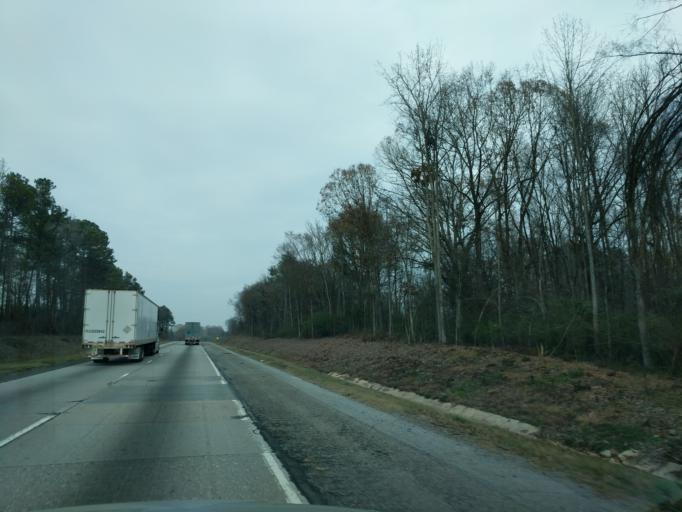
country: US
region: Georgia
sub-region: Jackson County
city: Commerce
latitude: 34.2748
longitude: -83.4352
